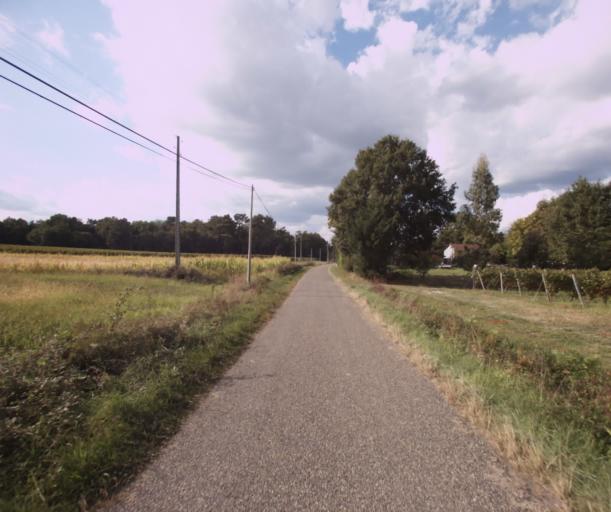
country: FR
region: Midi-Pyrenees
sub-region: Departement du Gers
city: Cazaubon
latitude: 43.8930
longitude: -0.0443
